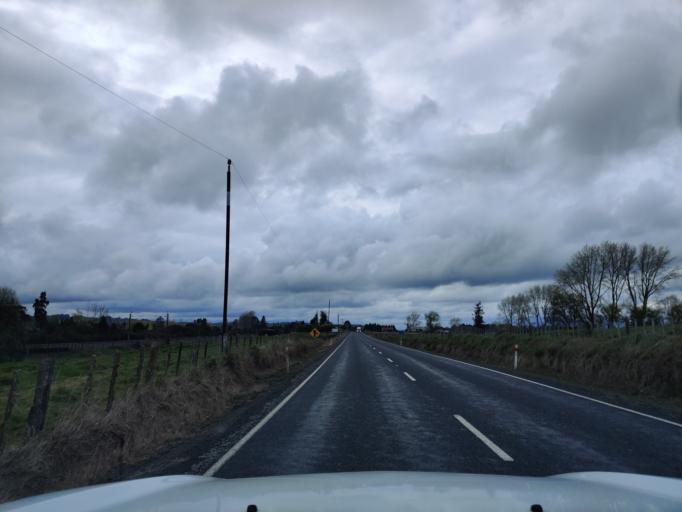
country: NZ
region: Waikato
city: Turangi
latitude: -39.0103
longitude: 175.3778
